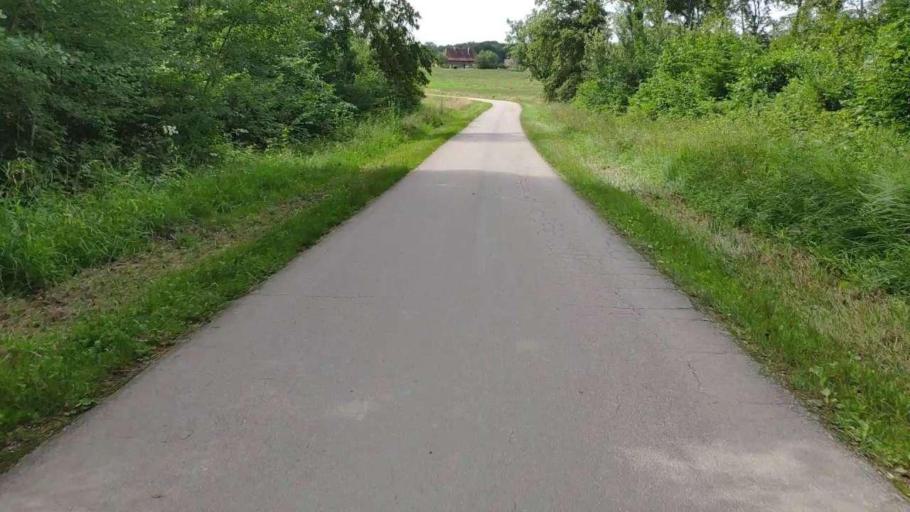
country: FR
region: Franche-Comte
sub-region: Departement du Jura
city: Bletterans
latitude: 46.8150
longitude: 5.4334
